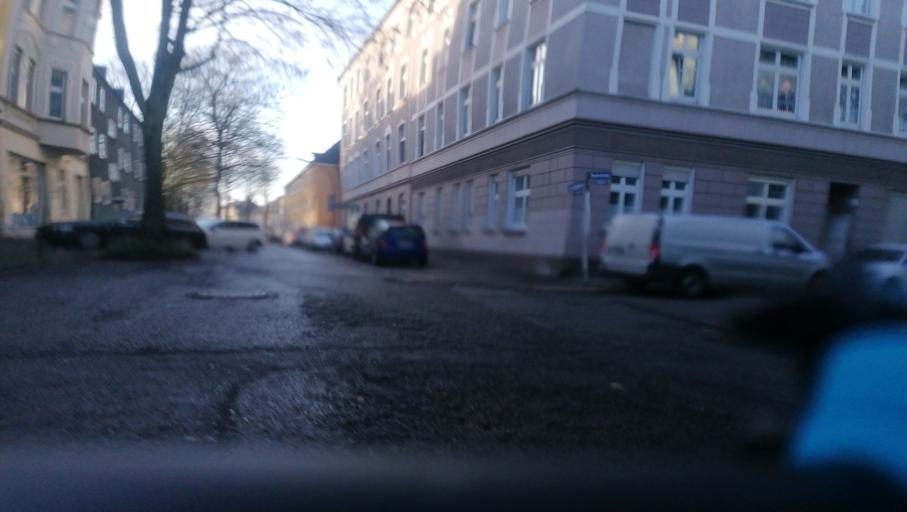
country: DE
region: North Rhine-Westphalia
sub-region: Regierungsbezirk Arnsberg
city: Dortmund
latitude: 51.4816
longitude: 7.5014
